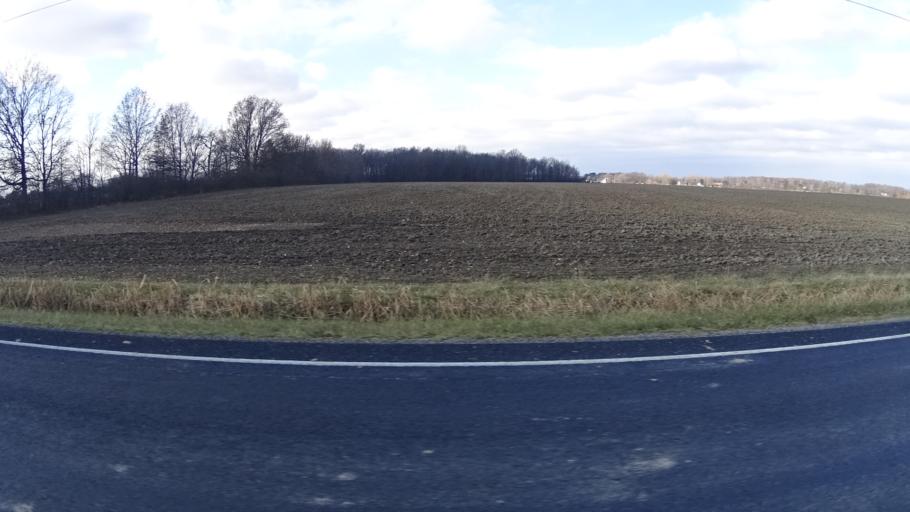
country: US
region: Ohio
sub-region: Lorain County
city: Camden
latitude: 41.2643
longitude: -82.2743
